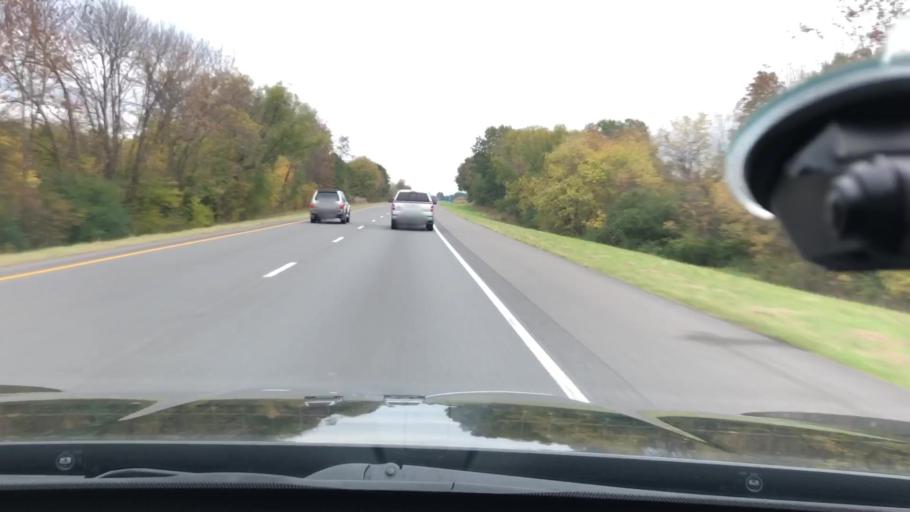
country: US
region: Arkansas
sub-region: Hempstead County
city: Hope
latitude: 33.7191
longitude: -93.5583
